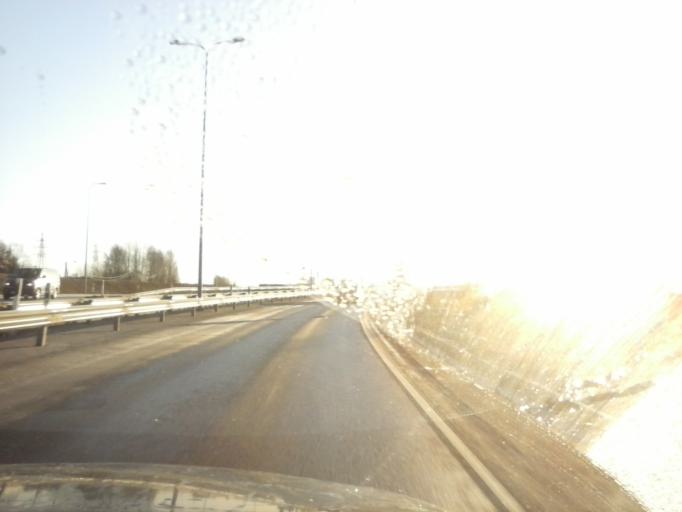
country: EE
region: Tartu
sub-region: UElenurme vald
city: Ulenurme
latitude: 58.3452
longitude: 26.7052
